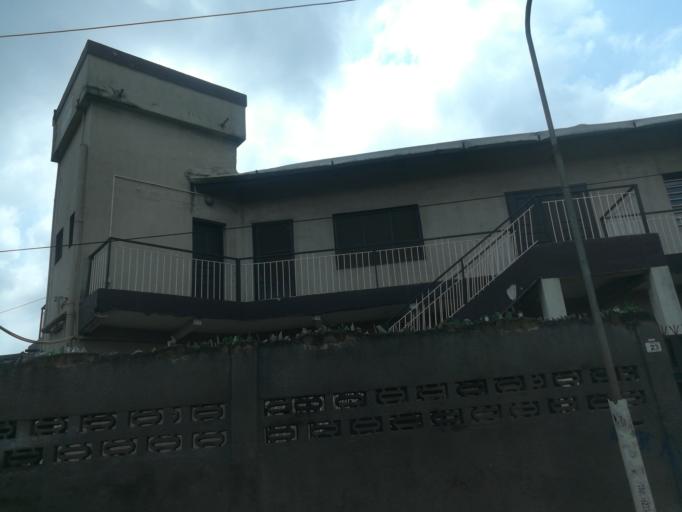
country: NG
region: Lagos
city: Mushin
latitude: 6.5319
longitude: 3.3641
